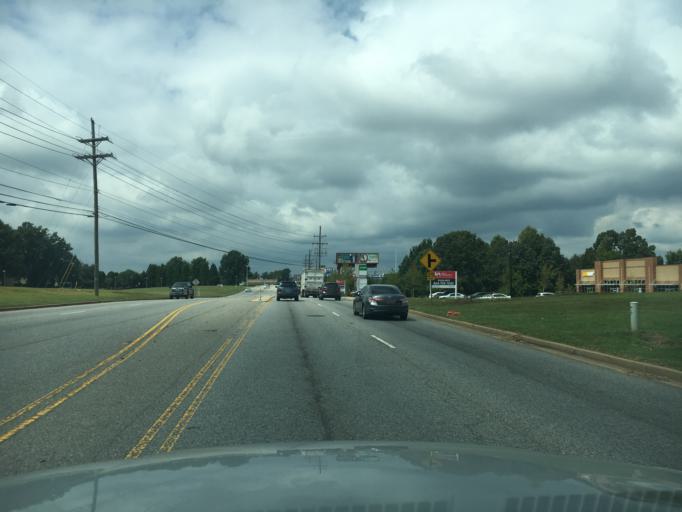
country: US
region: South Carolina
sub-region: Greenville County
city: Five Forks
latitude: 34.8556
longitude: -82.2514
